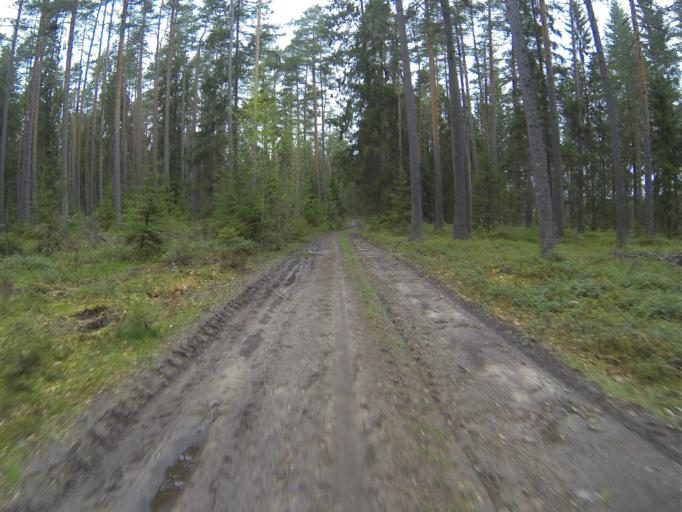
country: FI
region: Varsinais-Suomi
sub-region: Salo
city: Pertteli
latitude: 60.3999
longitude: 23.2058
